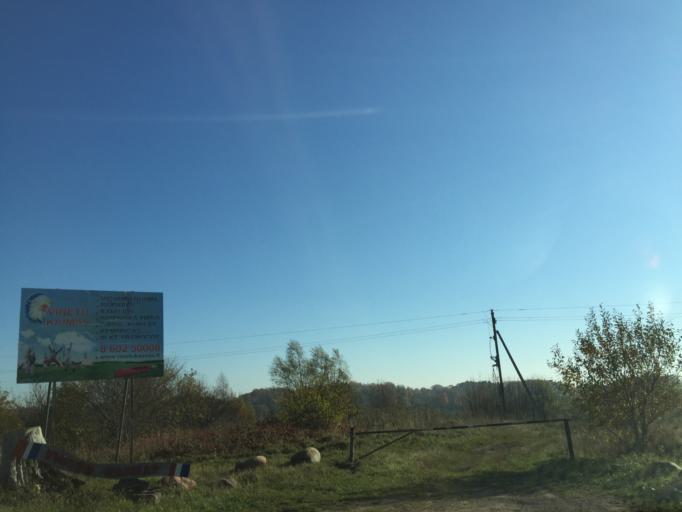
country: LT
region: Klaipedos apskritis
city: Kretinga
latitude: 55.8508
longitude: 21.2163
